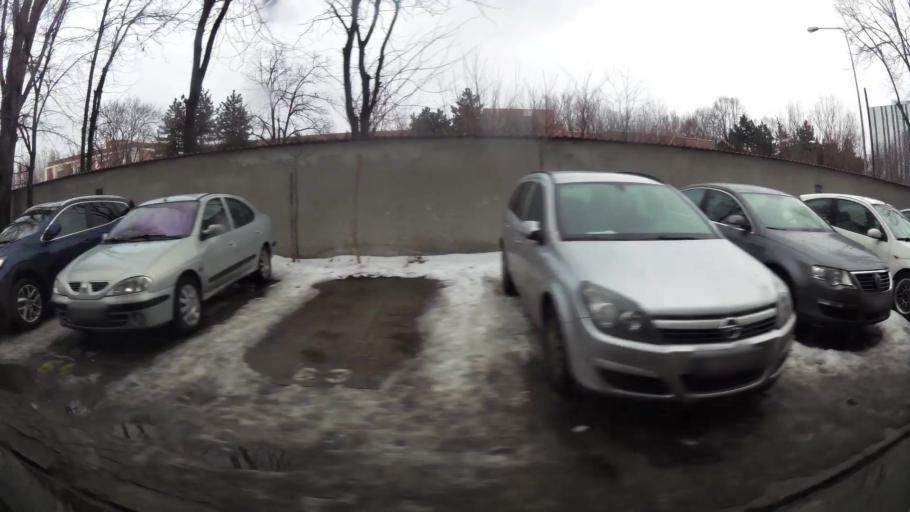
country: RO
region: Ilfov
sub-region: Comuna Chiajna
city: Rosu
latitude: 44.4362
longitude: 26.0449
